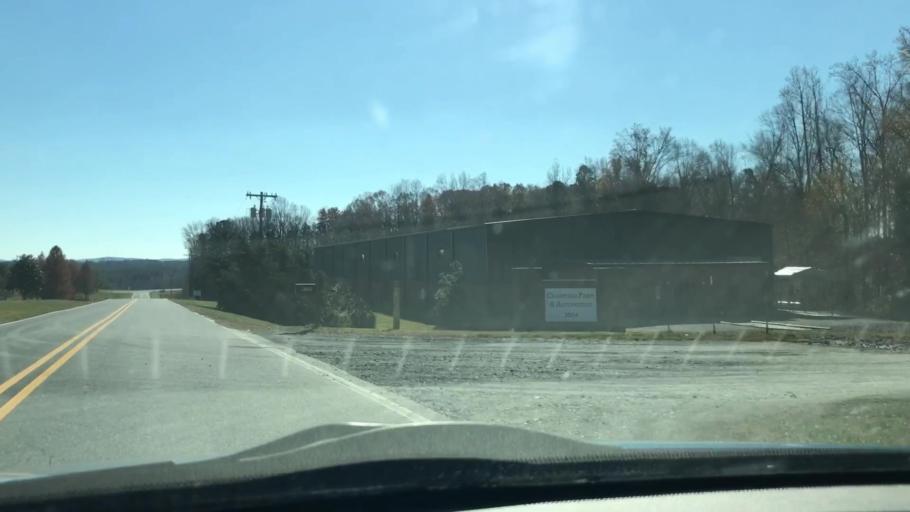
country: US
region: North Carolina
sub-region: Davidson County
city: Denton
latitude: 35.6435
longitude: -79.9732
